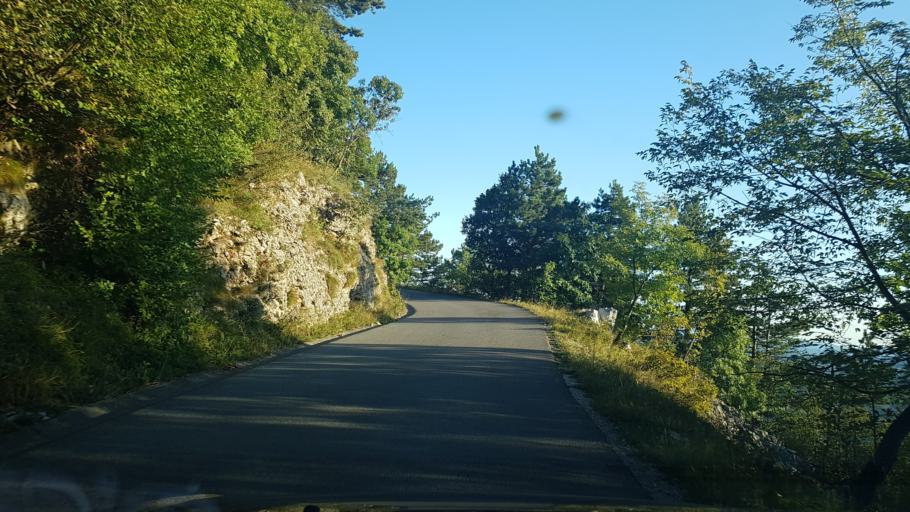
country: SI
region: Vipava
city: Vipava
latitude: 45.7994
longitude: 14.0043
